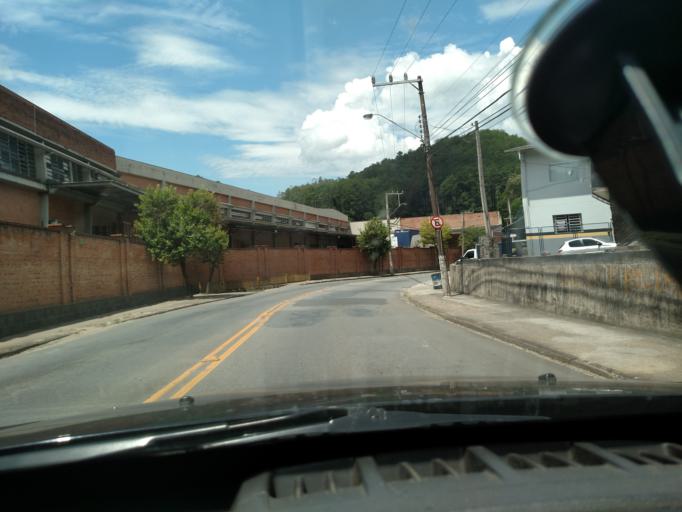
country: BR
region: Santa Catarina
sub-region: Blumenau
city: Blumenau
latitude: -26.9608
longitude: -49.0690
